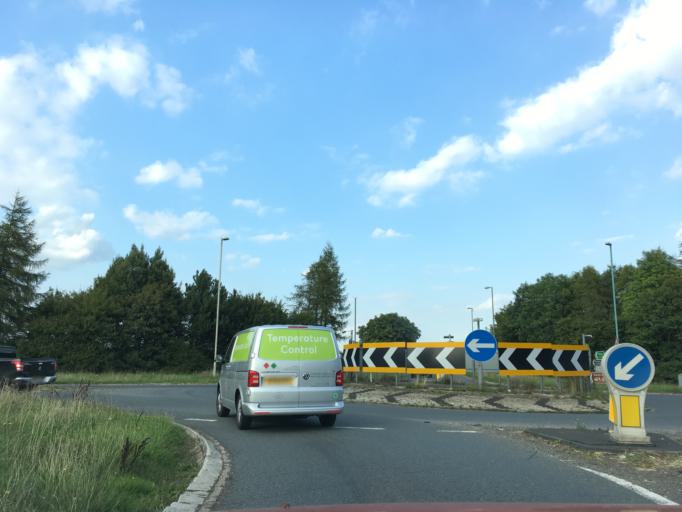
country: GB
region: England
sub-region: Gloucestershire
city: Northleach
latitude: 51.8378
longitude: -1.8362
